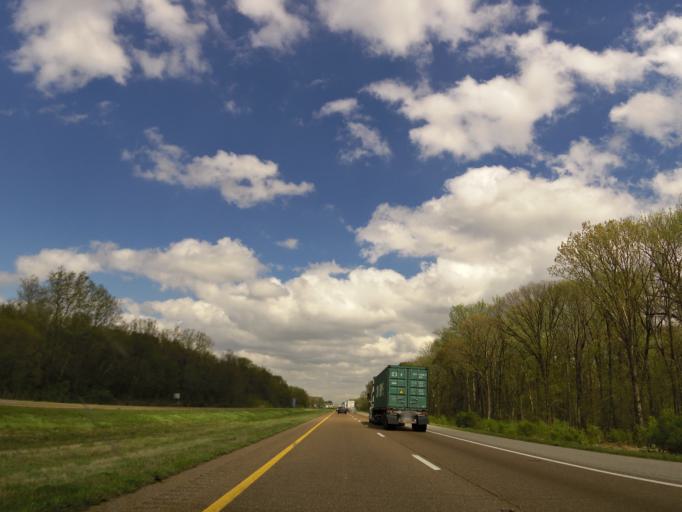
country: US
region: Tennessee
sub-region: Tipton County
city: Mason
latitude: 35.3394
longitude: -89.5387
